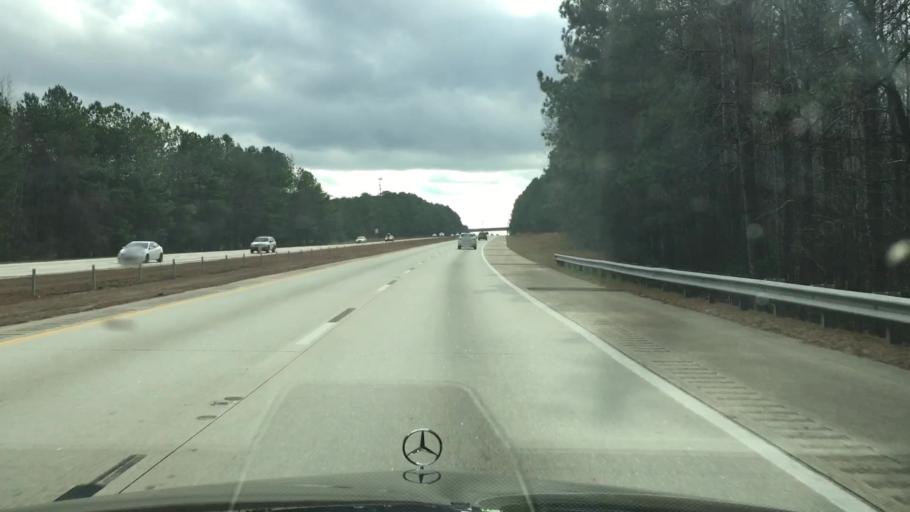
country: US
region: North Carolina
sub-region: Wake County
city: Garner
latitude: 35.6720
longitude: -78.5634
